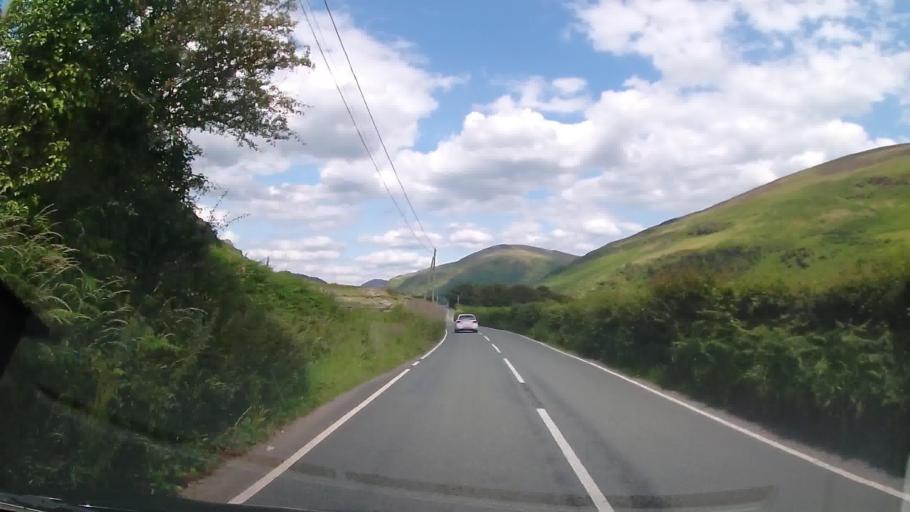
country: GB
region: Wales
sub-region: Gwynedd
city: Tywyn
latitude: 52.6156
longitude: -4.0223
